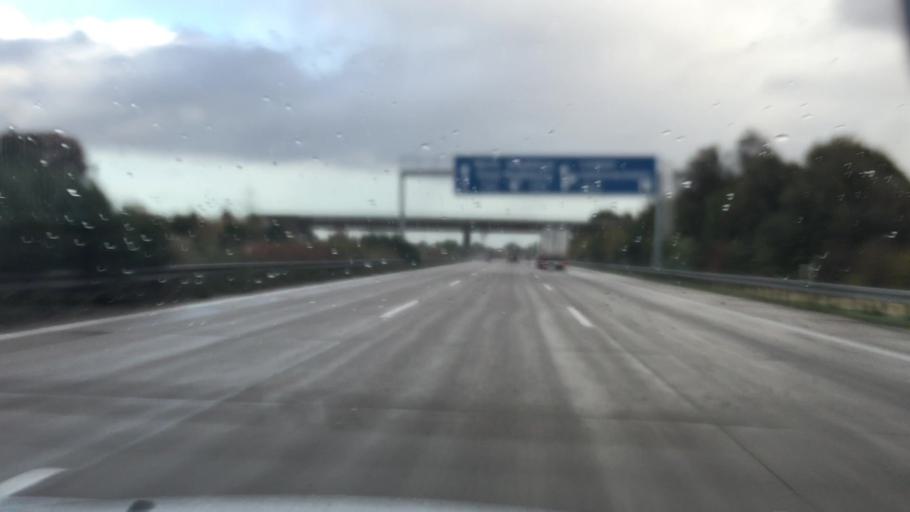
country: DE
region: Saxony-Anhalt
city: Hermsdorf
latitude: 52.1784
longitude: 11.4728
